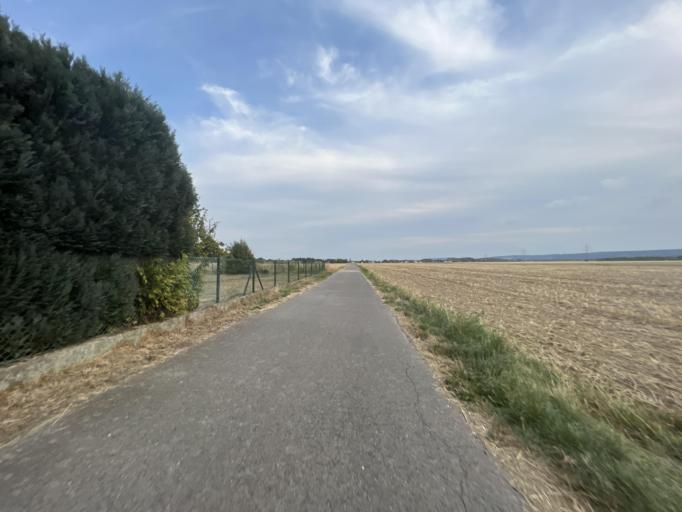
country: DE
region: North Rhine-Westphalia
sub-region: Regierungsbezirk Koln
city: Dueren
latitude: 50.8285
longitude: 6.4353
